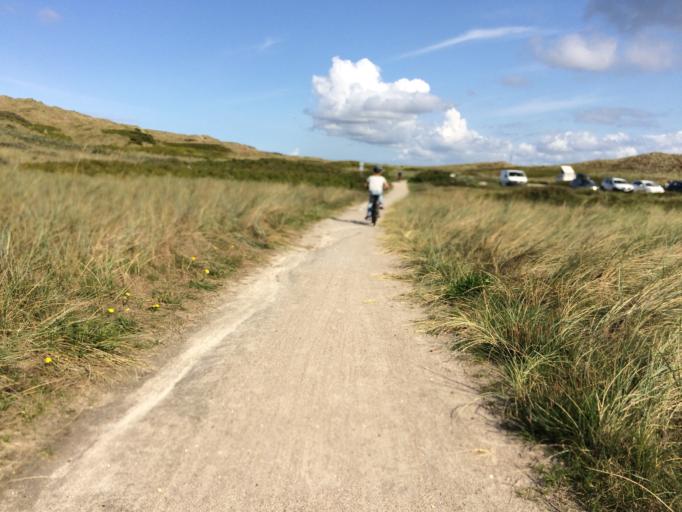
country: DK
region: Central Jutland
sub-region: Ringkobing-Skjern Kommune
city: Hvide Sande
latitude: 55.9383
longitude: 8.1491
